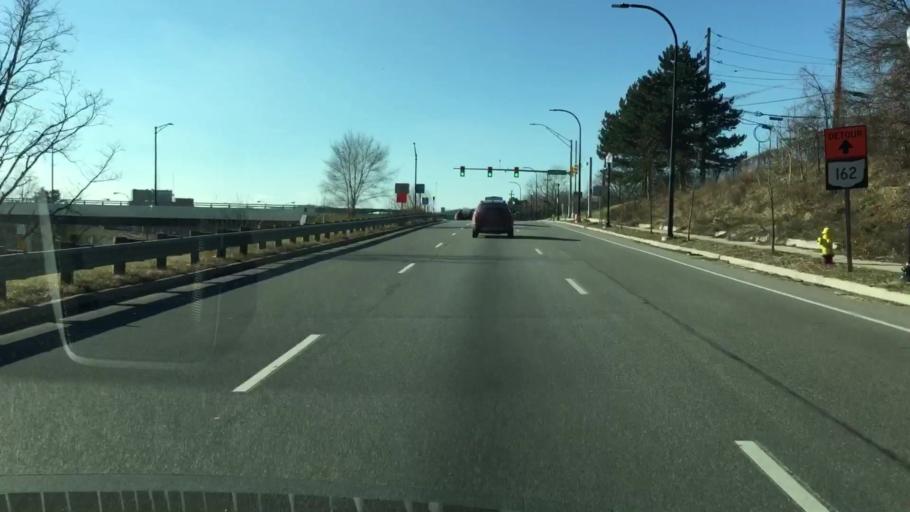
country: US
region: Ohio
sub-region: Summit County
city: Akron
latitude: 41.0827
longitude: -81.5240
